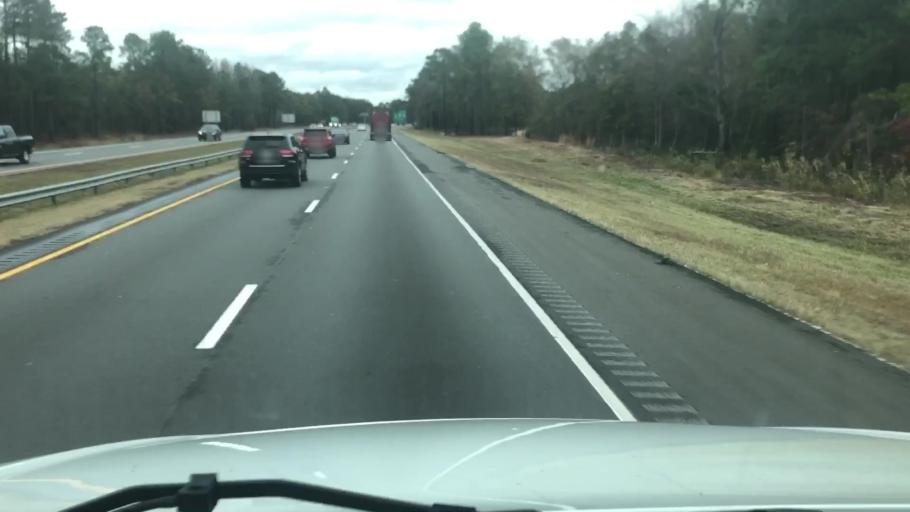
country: US
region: North Carolina
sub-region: Cumberland County
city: Eastover
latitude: 35.1070
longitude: -78.7696
